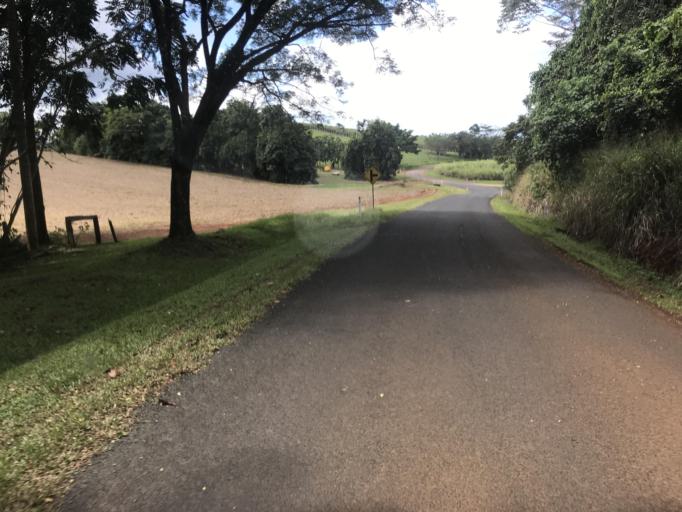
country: AU
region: Queensland
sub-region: Cassowary Coast
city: Innisfail
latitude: -17.5494
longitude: 145.8686
